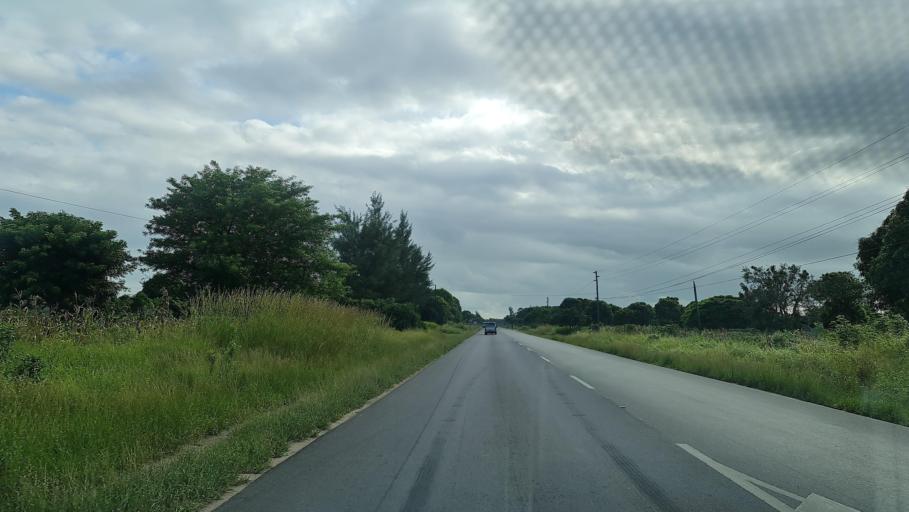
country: MZ
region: Maputo
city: Manhica
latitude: -25.4166
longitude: 32.7348
